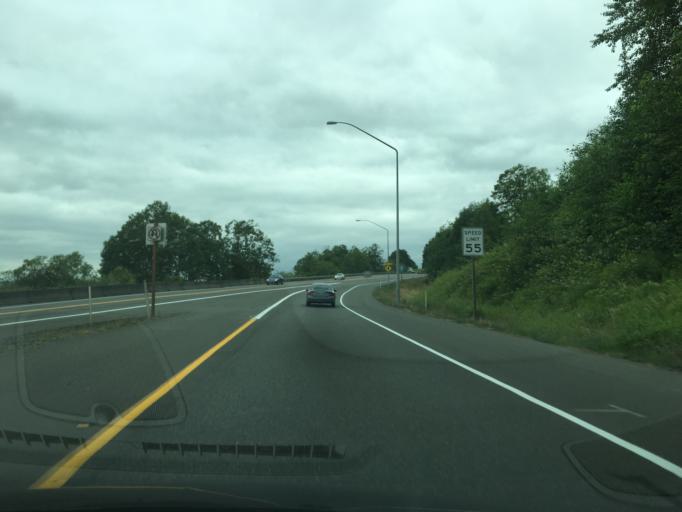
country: US
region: Washington
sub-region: Snohomish County
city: Fobes Hill
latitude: 47.9801
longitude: -122.1374
